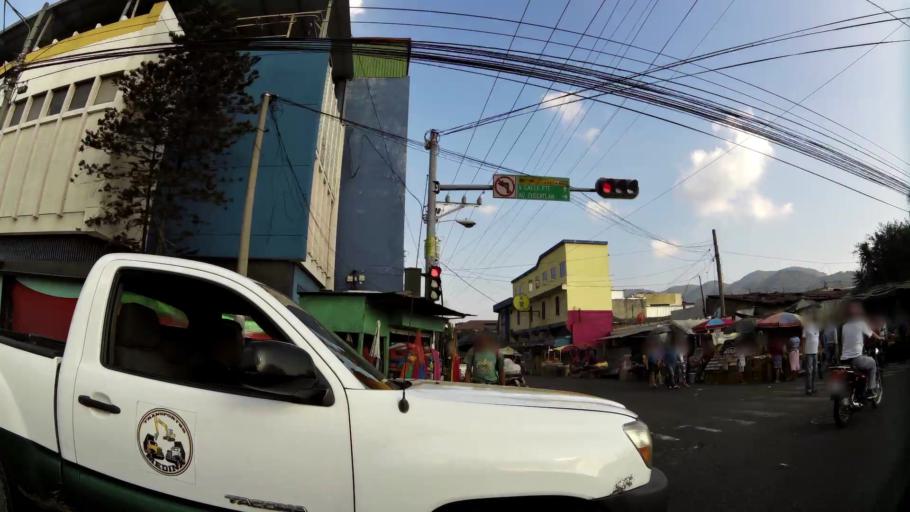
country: SV
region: San Salvador
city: San Salvador
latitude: 13.6964
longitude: -89.1917
